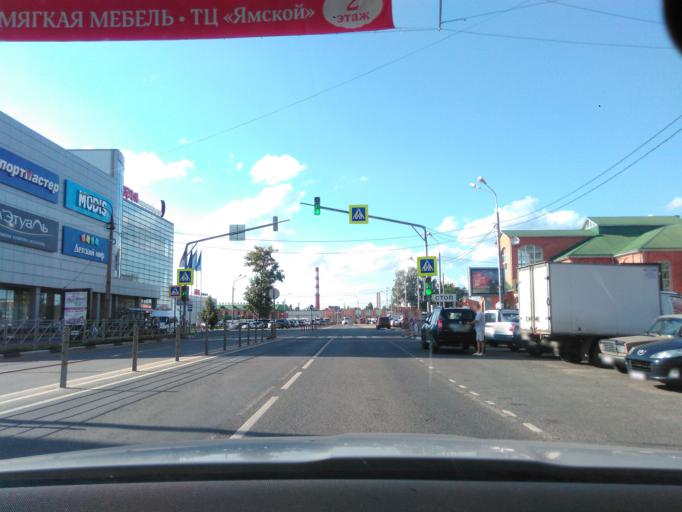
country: RU
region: Moskovskaya
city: Klin
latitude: 56.3316
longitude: 36.7142
